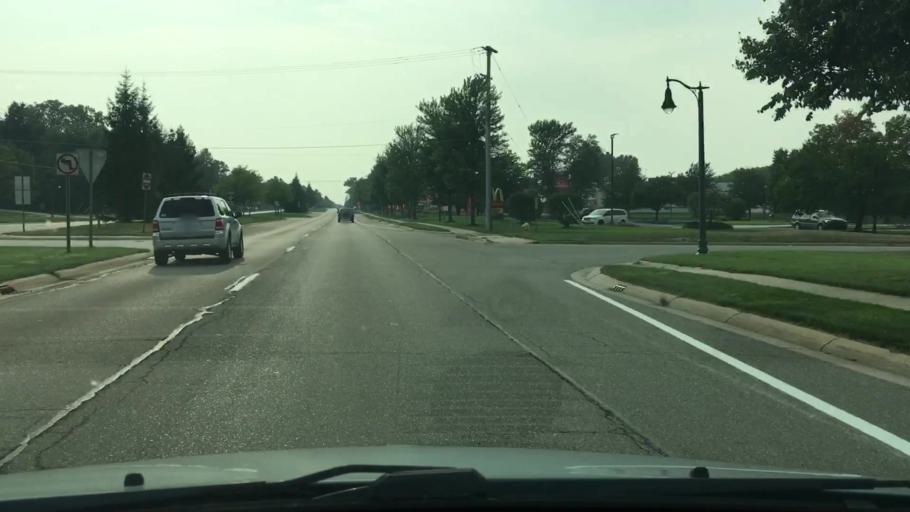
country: US
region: Michigan
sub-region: Ottawa County
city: Allendale
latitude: 42.9725
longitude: -85.9147
